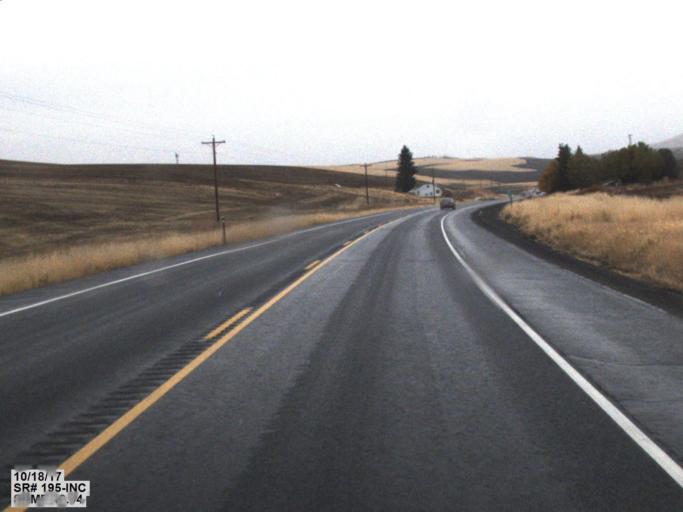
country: US
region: Washington
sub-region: Whitman County
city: Colfax
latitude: 46.9447
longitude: -117.3353
